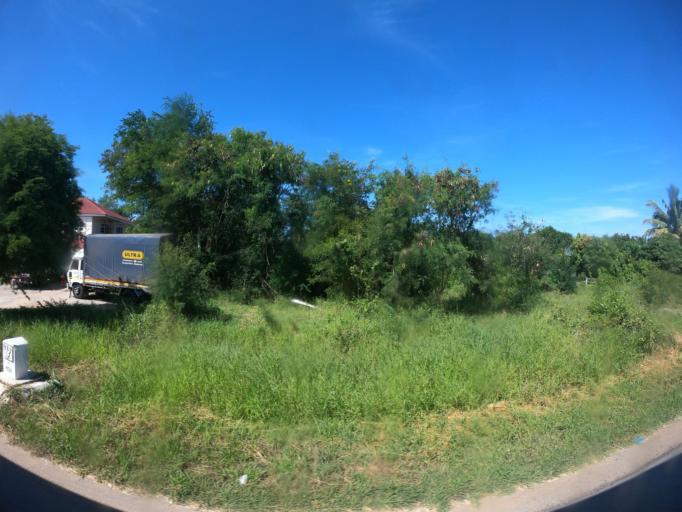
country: TH
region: Nakhon Ratchasima
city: Nakhon Ratchasima
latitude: 15.0520
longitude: 102.1565
